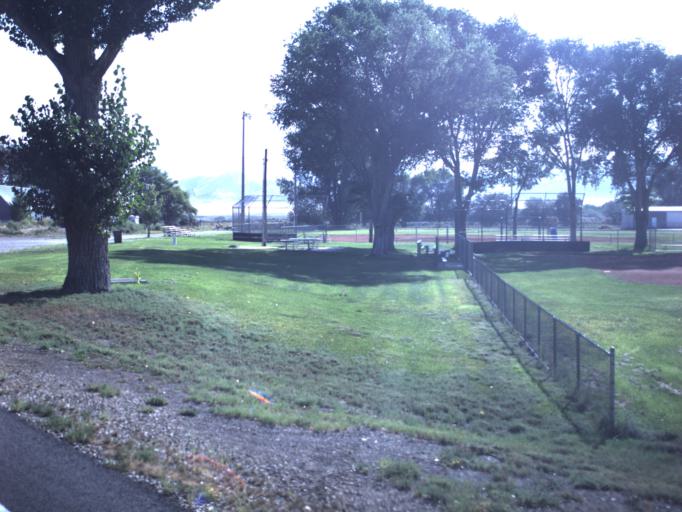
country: US
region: Utah
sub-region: Sevier County
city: Salina
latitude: 39.0079
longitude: -111.8596
